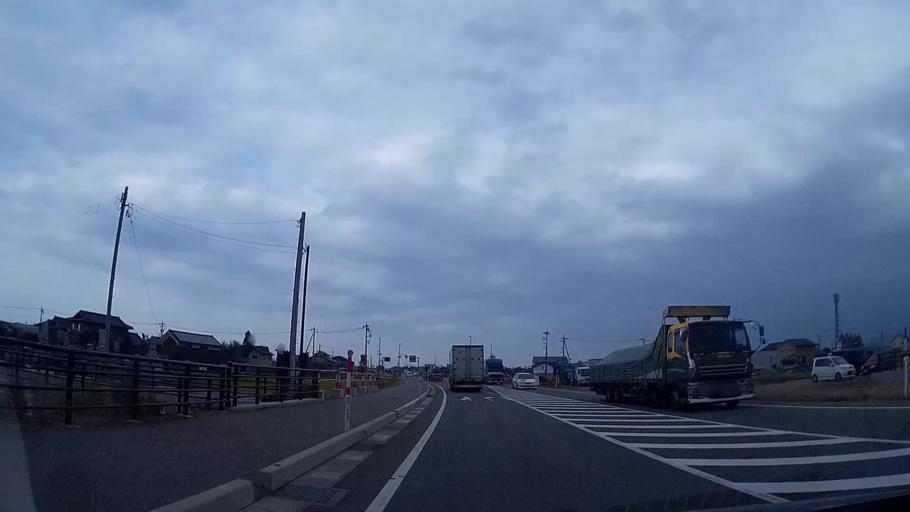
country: JP
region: Toyama
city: Nyuzen
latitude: 36.8909
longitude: 137.4440
